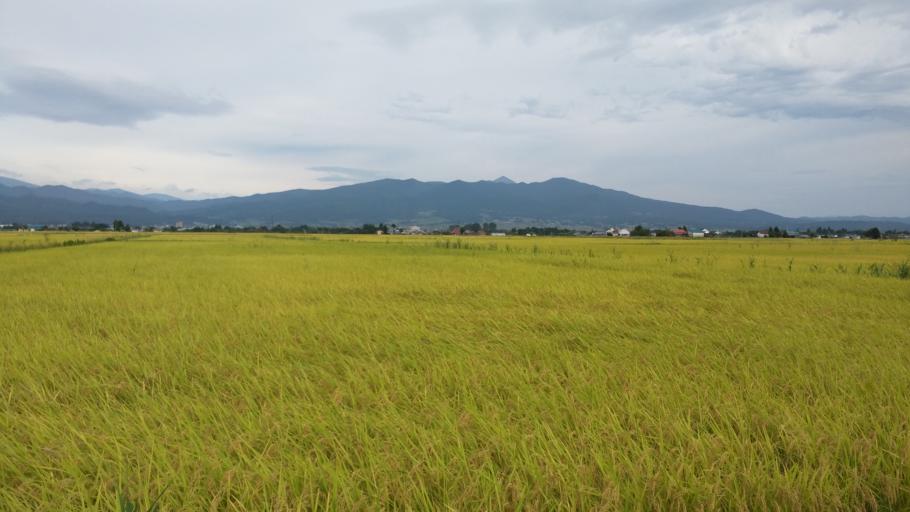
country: JP
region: Fukushima
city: Kitakata
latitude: 37.6424
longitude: 139.8408
